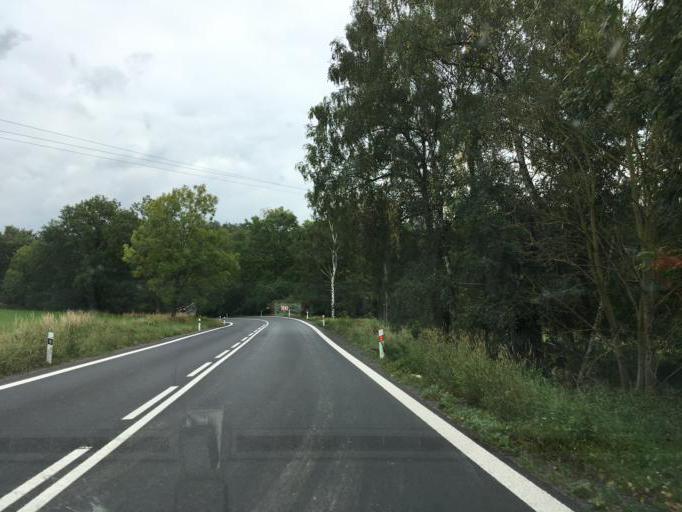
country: CZ
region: Vysocina
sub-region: Okres Pelhrimov
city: Zeliv
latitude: 49.5546
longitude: 15.1248
